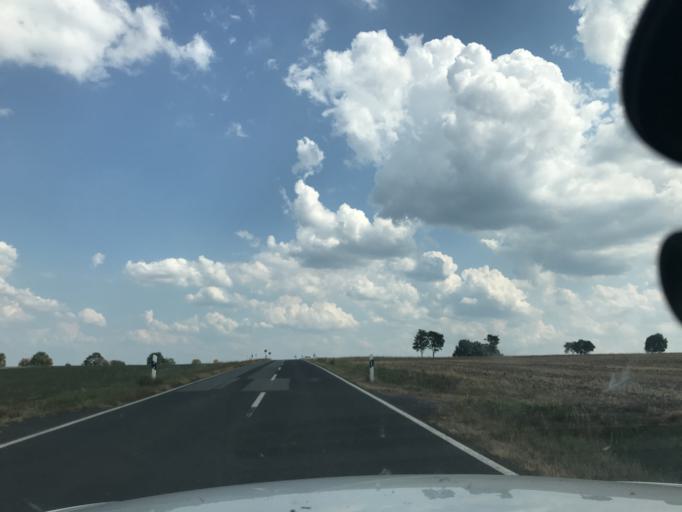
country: DE
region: Bavaria
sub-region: Upper Palatinate
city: Kirchenthumbach
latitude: 49.7624
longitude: 11.6891
